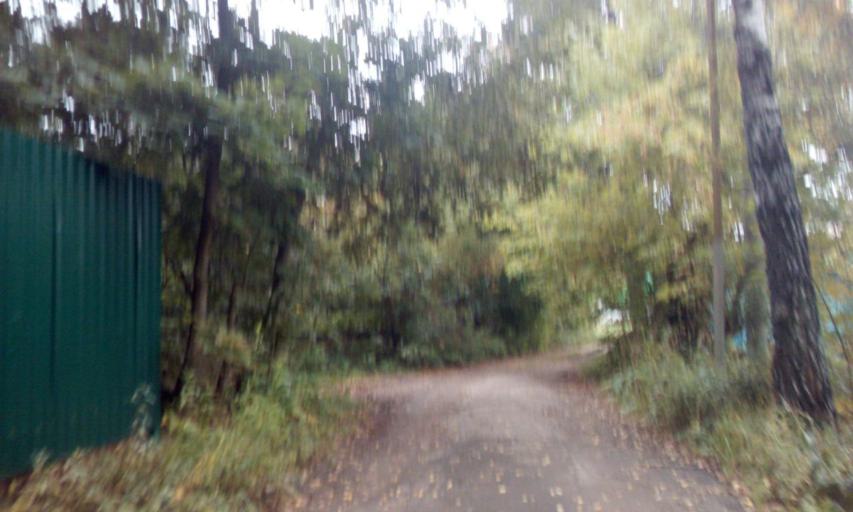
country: RU
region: Moskovskaya
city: Zhavoronki
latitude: 55.6439
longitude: 37.1060
